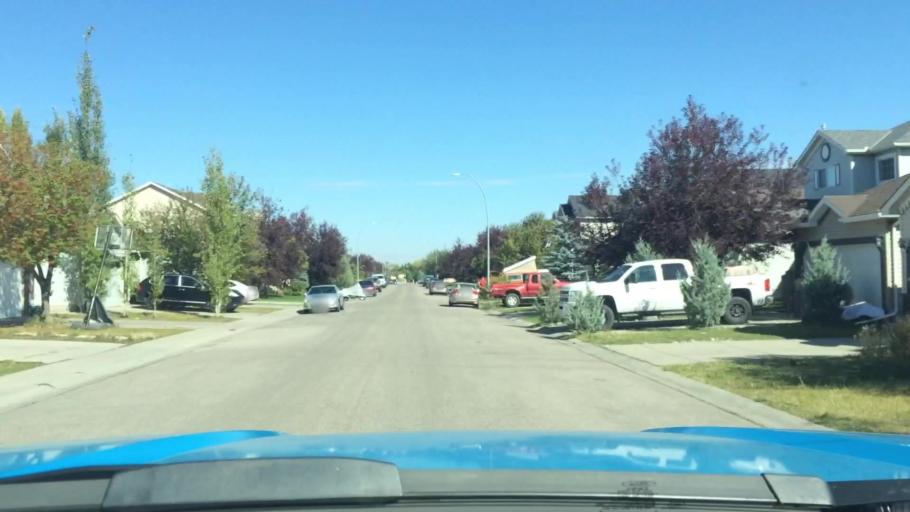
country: CA
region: Alberta
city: Calgary
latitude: 50.9041
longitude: -114.1091
